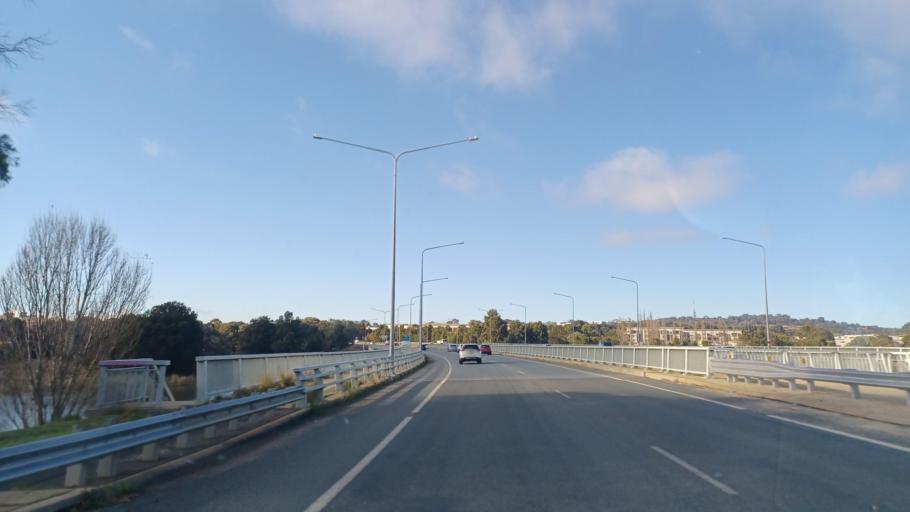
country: AU
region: Australian Capital Territory
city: Belconnen
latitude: -35.2287
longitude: 149.0762
